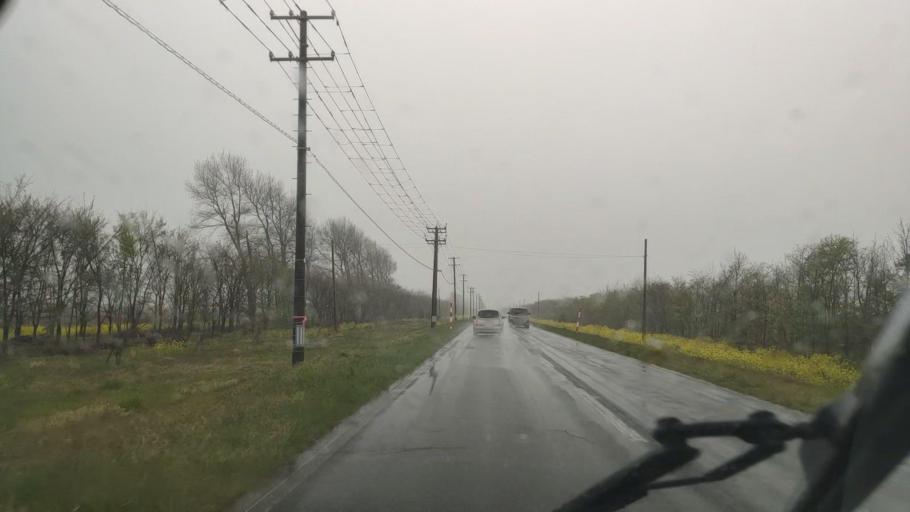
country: JP
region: Akita
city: Tenno
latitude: 39.9693
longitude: 139.9462
